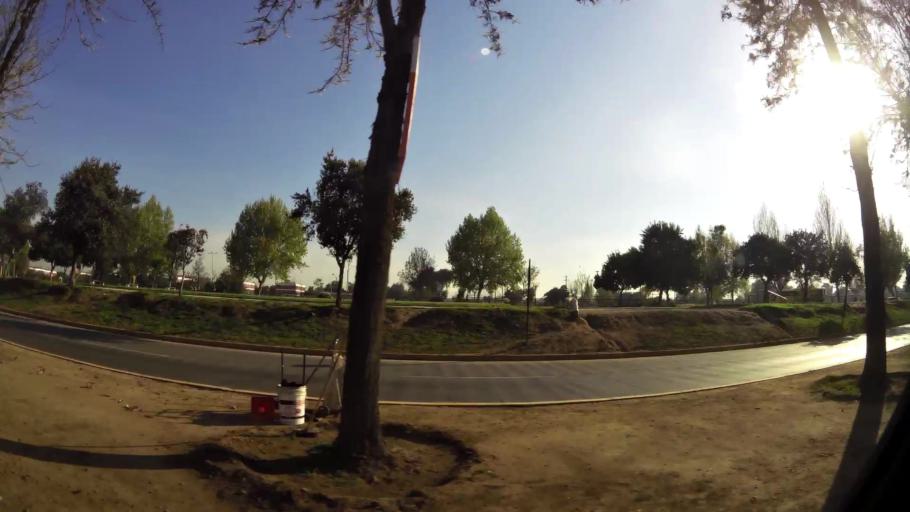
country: CL
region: Santiago Metropolitan
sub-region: Provincia de Santiago
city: Lo Prado
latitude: -33.4542
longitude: -70.7395
